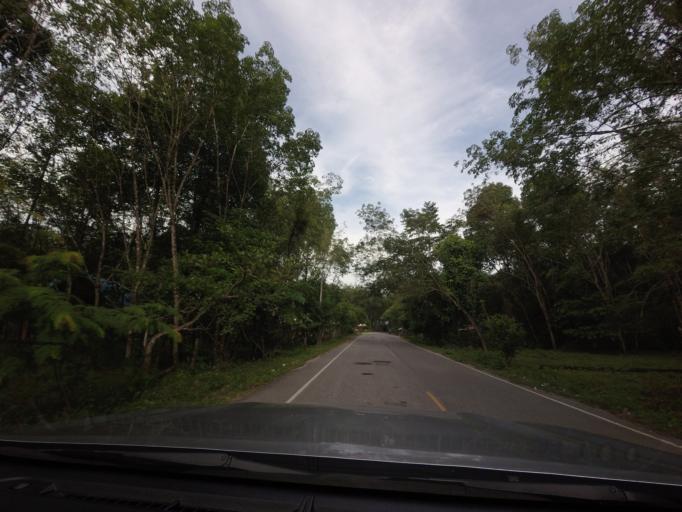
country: TH
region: Narathiwat
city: Rueso
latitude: 6.3511
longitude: 101.4744
